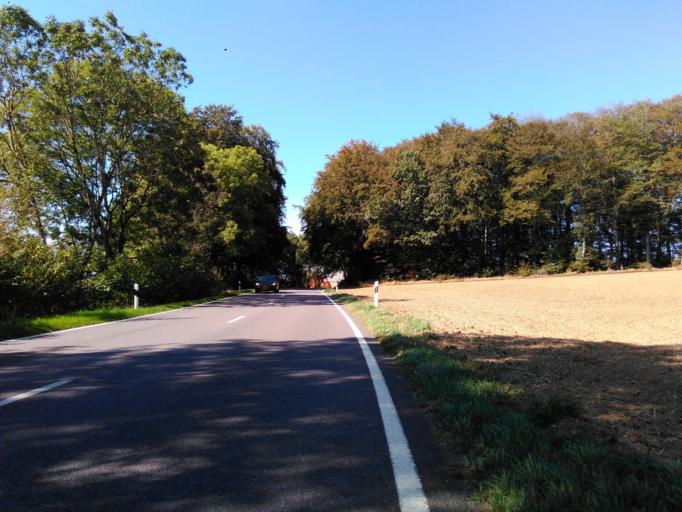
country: LU
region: Diekirch
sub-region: Canton de Redange
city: Rambrouch
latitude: 49.8352
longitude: 5.8413
